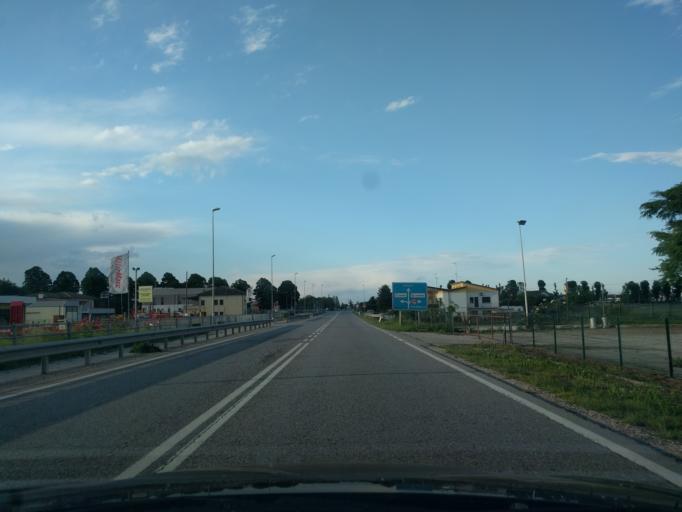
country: IT
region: Veneto
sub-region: Provincia di Rovigo
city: Polesella
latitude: 44.9589
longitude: 11.7400
